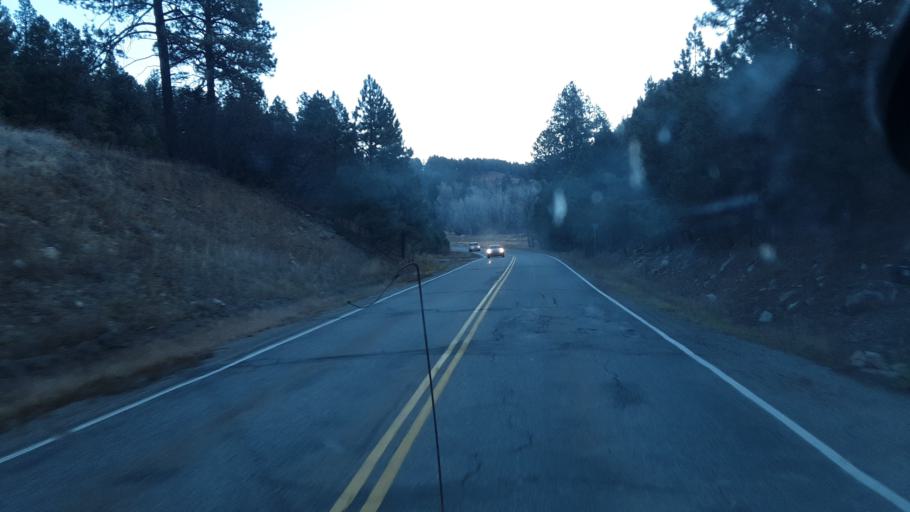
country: US
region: Colorado
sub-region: La Plata County
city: Durango
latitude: 37.3268
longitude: -107.7499
